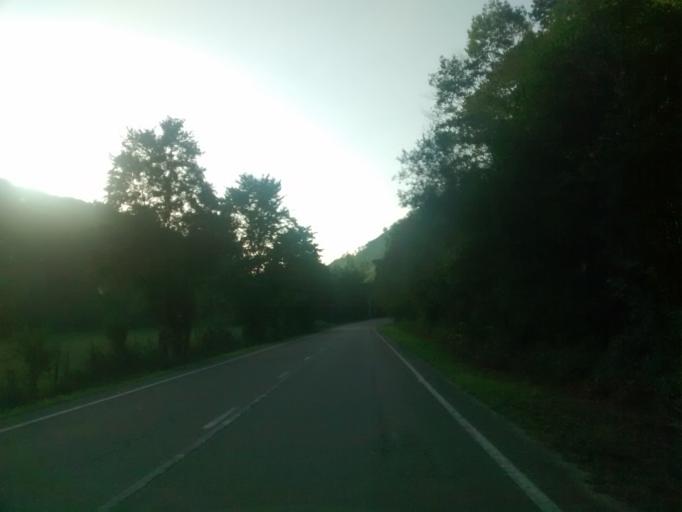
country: ES
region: Cantabria
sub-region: Provincia de Cantabria
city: Ruente
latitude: 43.1489
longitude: -4.2156
